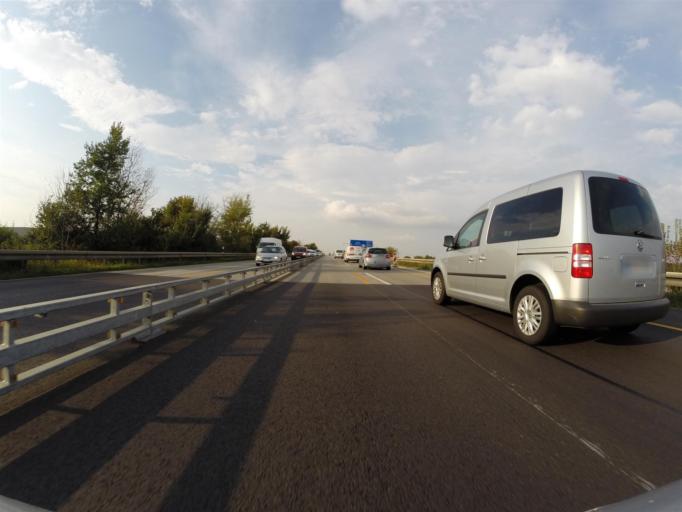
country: DE
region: Saxony-Anhalt
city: Osterfeld
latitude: 51.0812
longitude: 11.9554
